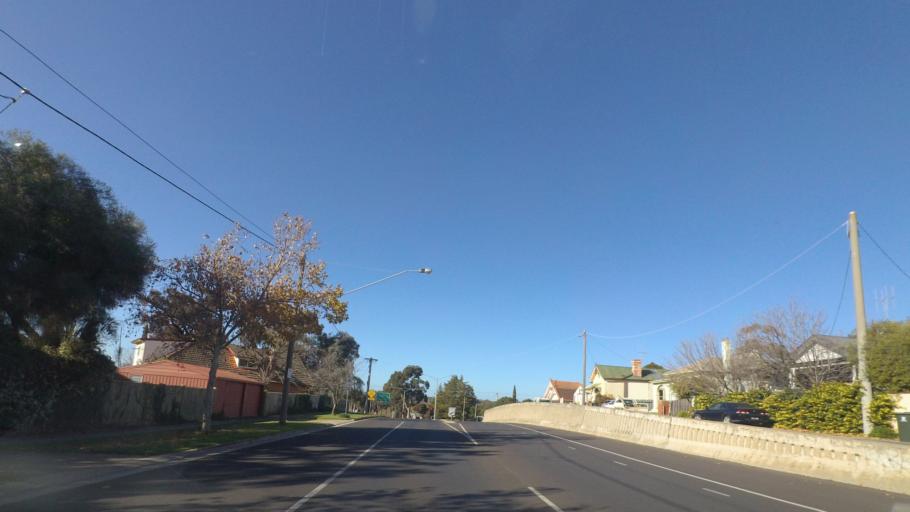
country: AU
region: Victoria
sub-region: Greater Bendigo
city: Quarry Hill
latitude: -36.7693
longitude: 144.2848
